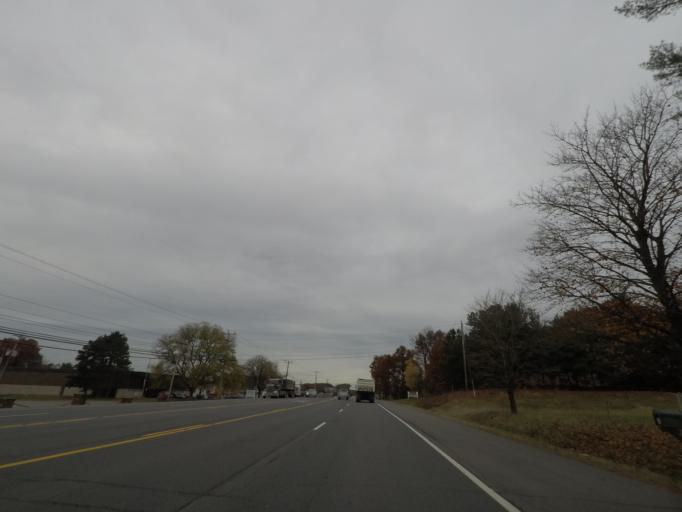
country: US
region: New York
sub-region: Saratoga County
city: Country Knolls
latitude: 42.8734
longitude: -73.7737
